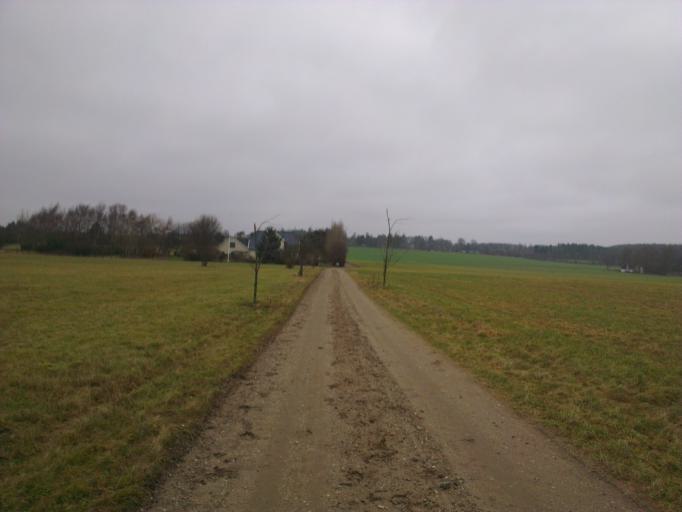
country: DK
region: Capital Region
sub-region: Frederikssund Kommune
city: Jaegerspris
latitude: 55.8421
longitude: 12.0072
